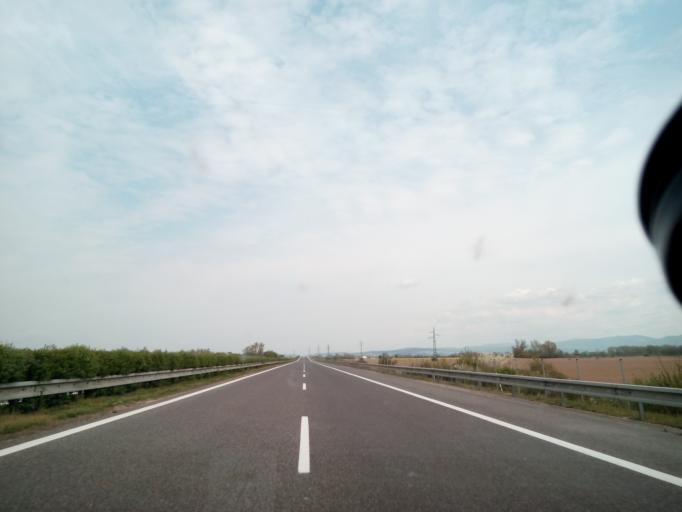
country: SK
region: Trenciansky
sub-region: Okres Nove Mesto nad Vahom
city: Nove Mesto nad Vahom
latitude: 48.8278
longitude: 17.9208
